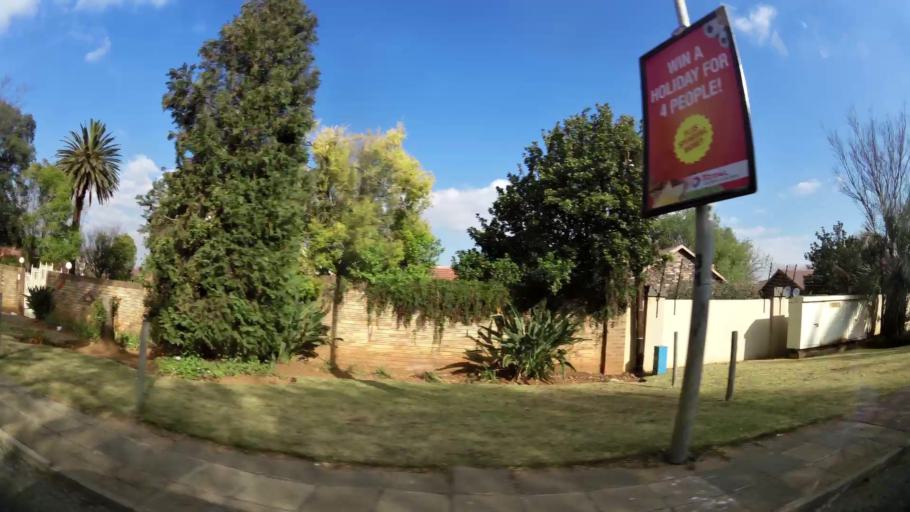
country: ZA
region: Gauteng
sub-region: West Rand District Municipality
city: Krugersdorp
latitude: -26.0872
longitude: 27.7747
